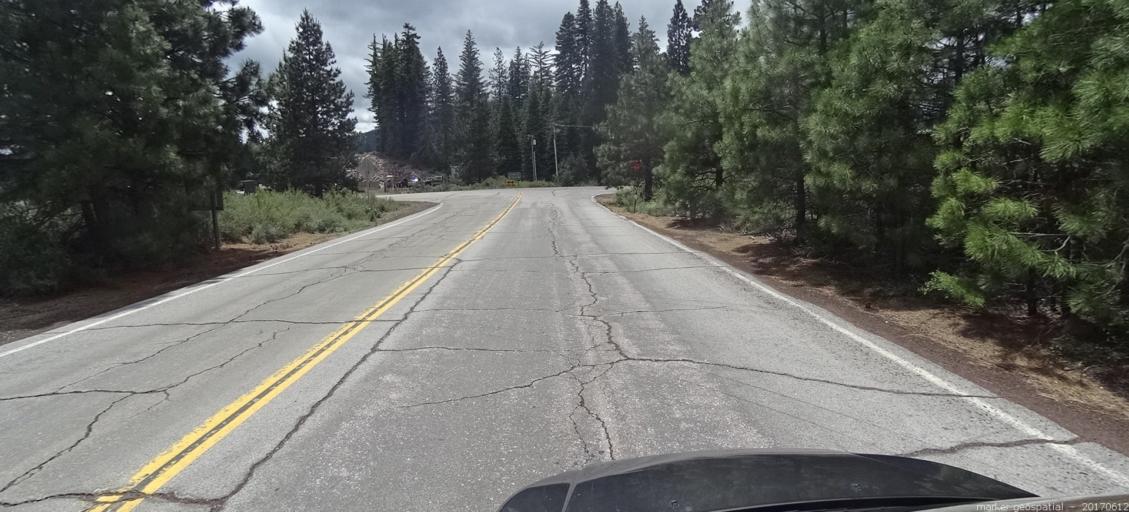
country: US
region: California
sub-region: Siskiyou County
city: Weed
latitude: 41.3677
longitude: -122.3713
